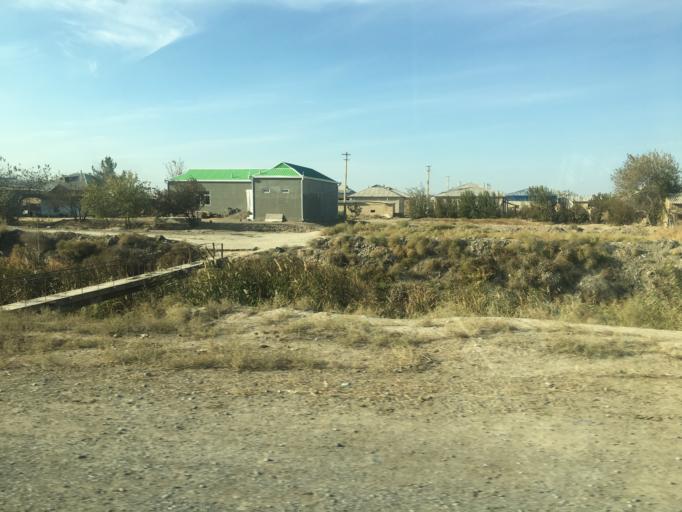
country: TM
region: Mary
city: Mary
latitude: 37.6066
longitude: 61.6929
